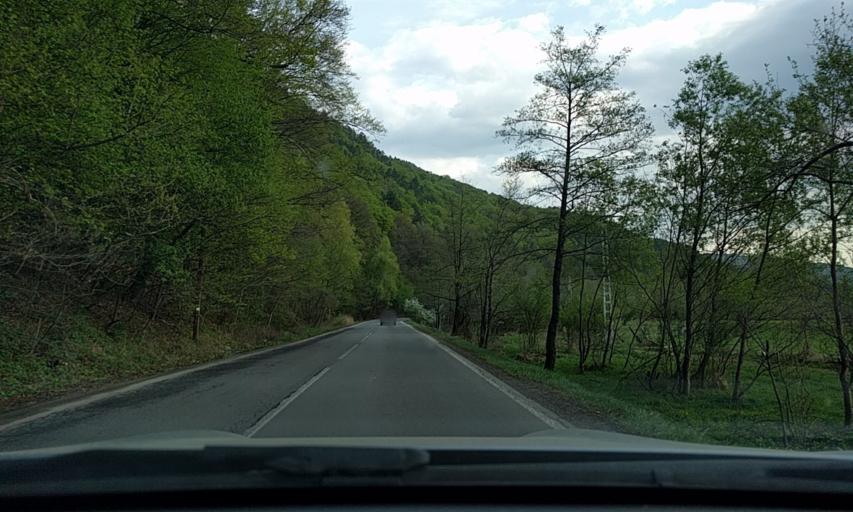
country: RO
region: Bacau
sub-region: Oras Slanic-Moldova
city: Slanic-Moldova
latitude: 46.1572
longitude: 26.4607
